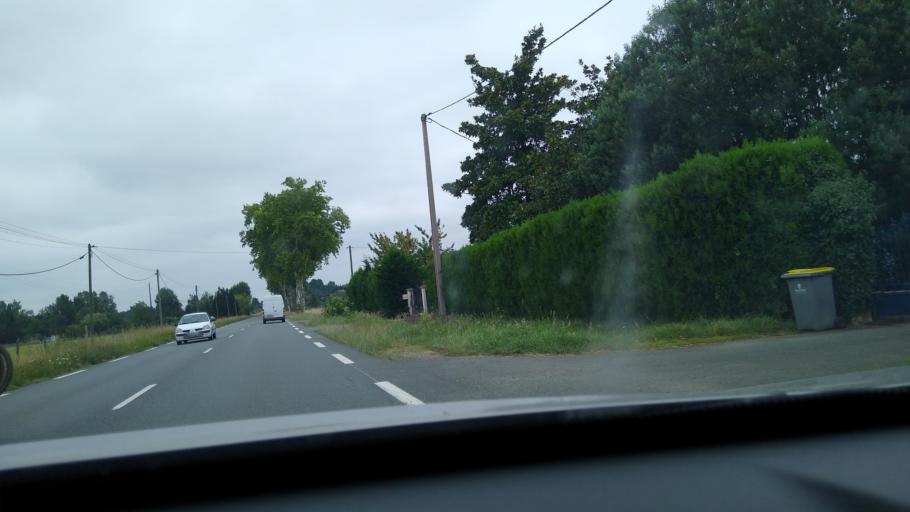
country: FR
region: Midi-Pyrenees
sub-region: Departement du Tarn
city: Brens
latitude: 43.8694
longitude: 1.9162
